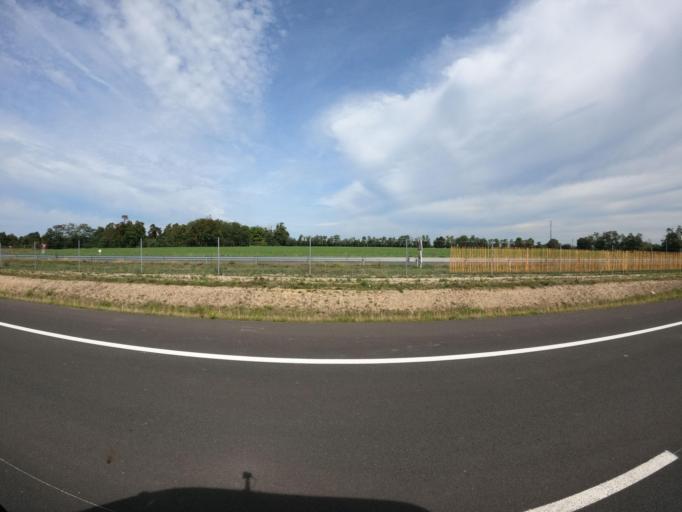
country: FR
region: Auvergne
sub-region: Departement de l'Allier
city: Beaulon
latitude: 46.5342
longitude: 3.5862
